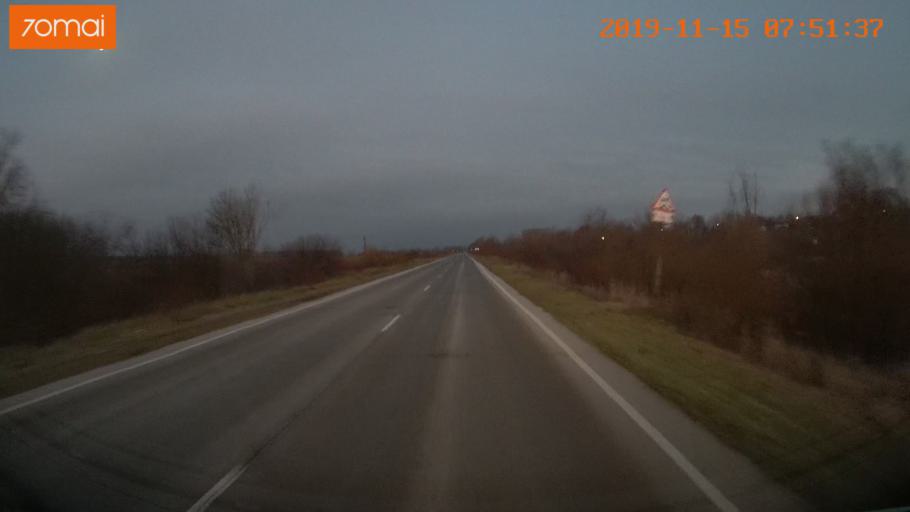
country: RU
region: Vologda
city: Cherepovets
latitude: 58.8807
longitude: 38.2013
